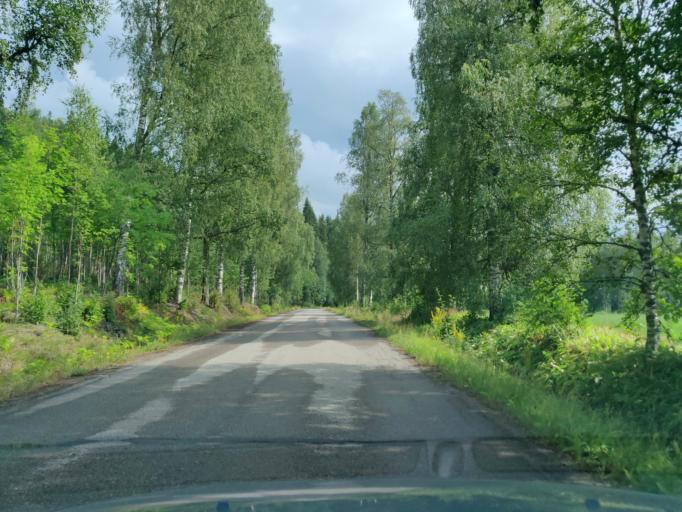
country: SE
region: Vaermland
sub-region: Hagfors Kommun
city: Hagfors
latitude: 60.0389
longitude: 13.5997
